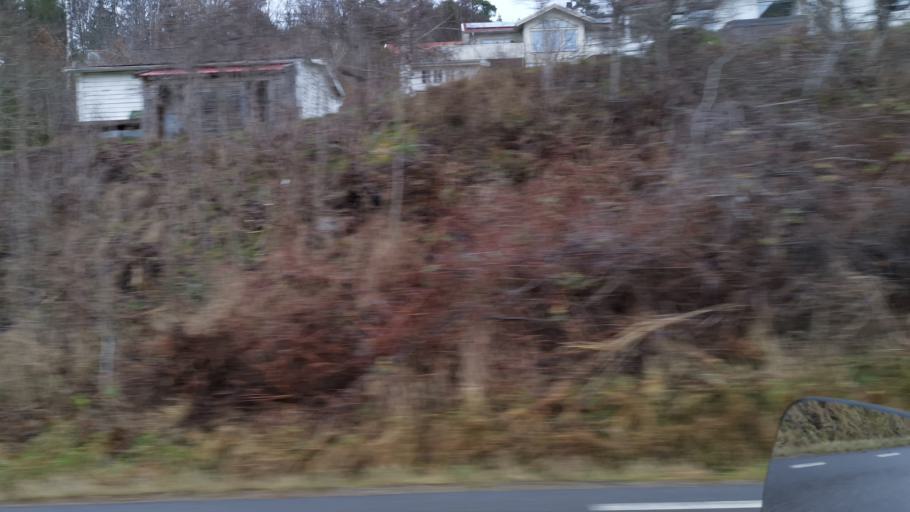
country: SE
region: Vaestra Goetaland
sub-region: Orust
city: Henan
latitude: 58.3404
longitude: 11.7062
